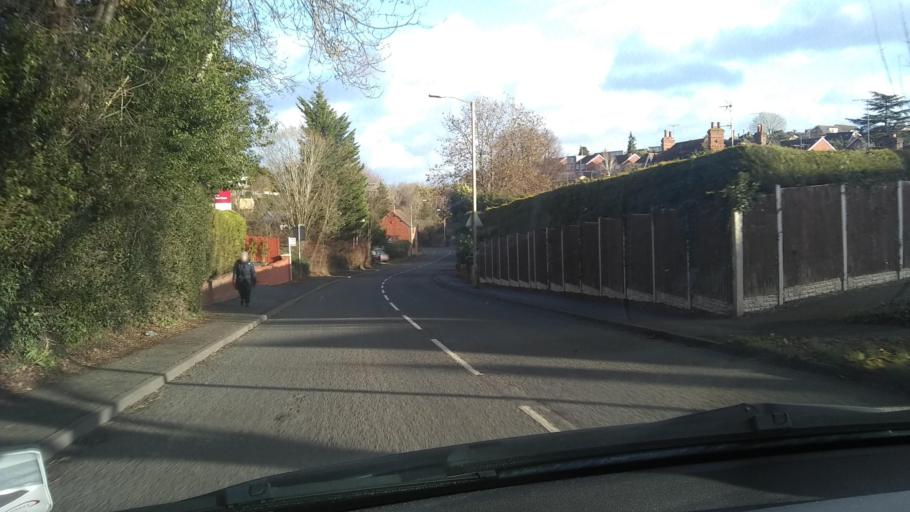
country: GB
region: England
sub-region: Worcestershire
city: Bewdley
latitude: 52.3754
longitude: -2.3279
